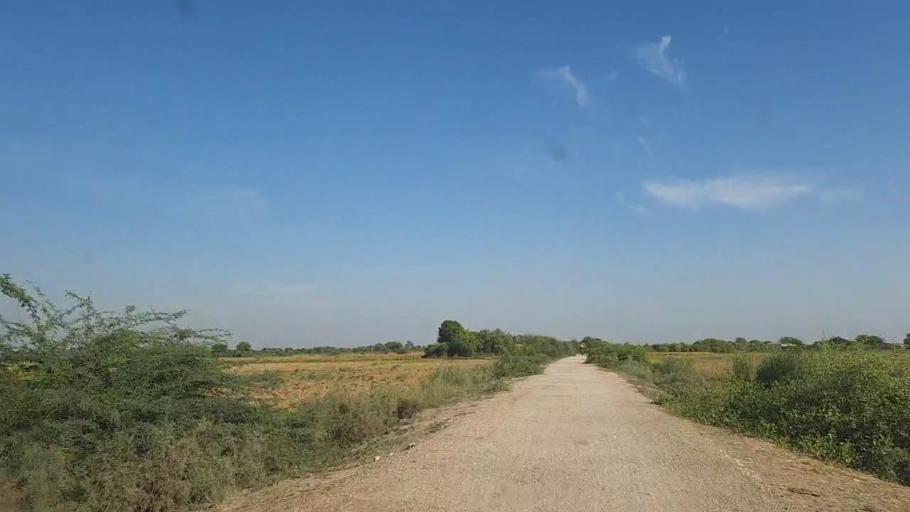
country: PK
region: Sindh
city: Mirpur Batoro
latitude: 24.7622
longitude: 68.3548
